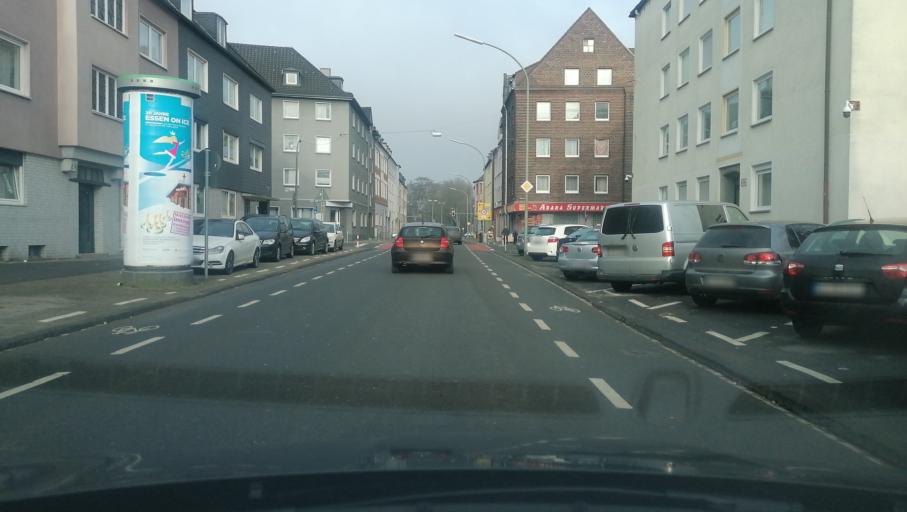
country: DE
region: North Rhine-Westphalia
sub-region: Regierungsbezirk Munster
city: Gelsenkirchen
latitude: 51.5151
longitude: 7.1098
